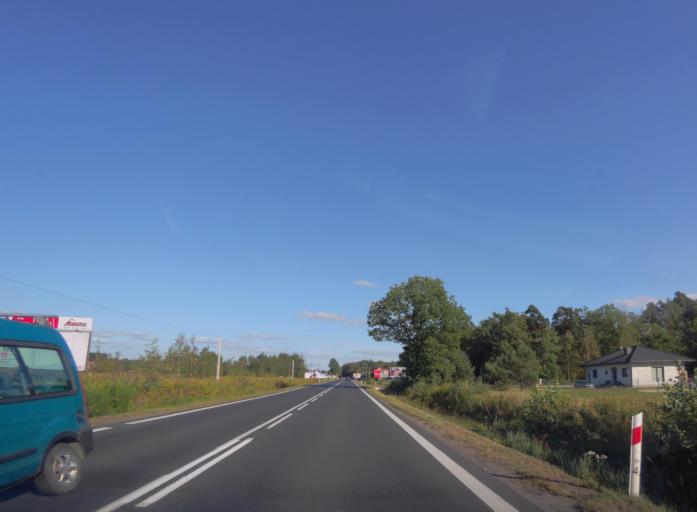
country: PL
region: Subcarpathian Voivodeship
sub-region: Powiat tarnobrzeski
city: Grebow
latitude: 50.5737
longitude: 21.9314
